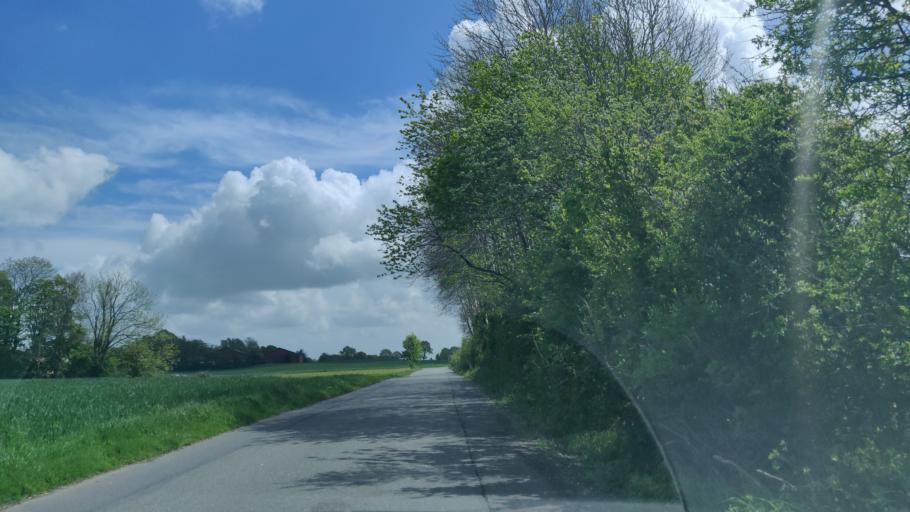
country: DK
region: South Denmark
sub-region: Vejle Kommune
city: Vejle
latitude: 55.6521
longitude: 9.5417
